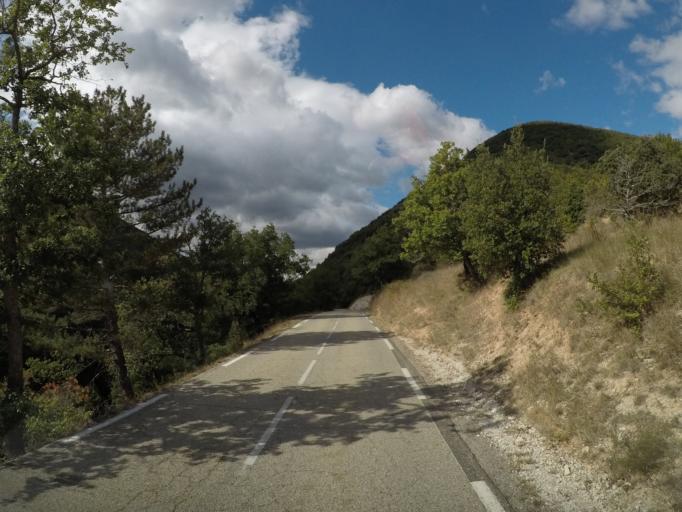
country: FR
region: Provence-Alpes-Cote d'Azur
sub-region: Departement du Vaucluse
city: Sault
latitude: 44.1854
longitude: 5.3492
